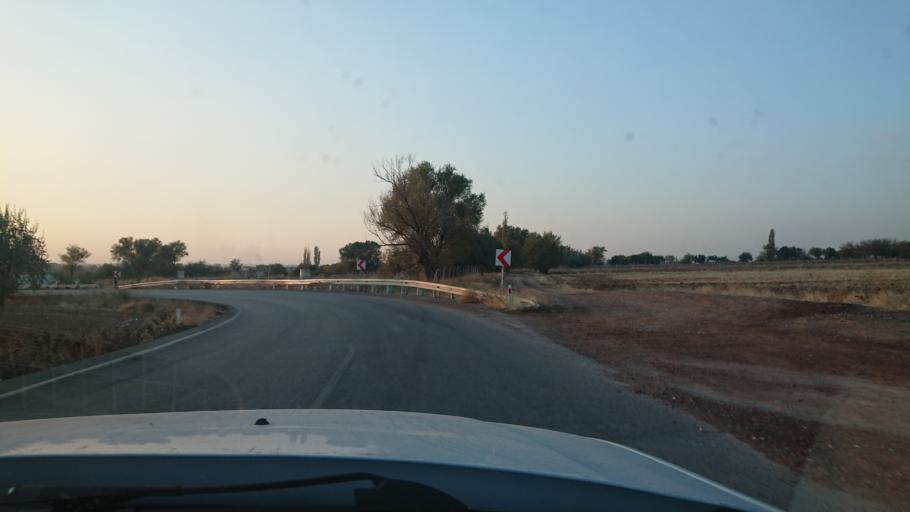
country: TR
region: Aksaray
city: Aksaray
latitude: 38.3009
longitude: 34.0820
